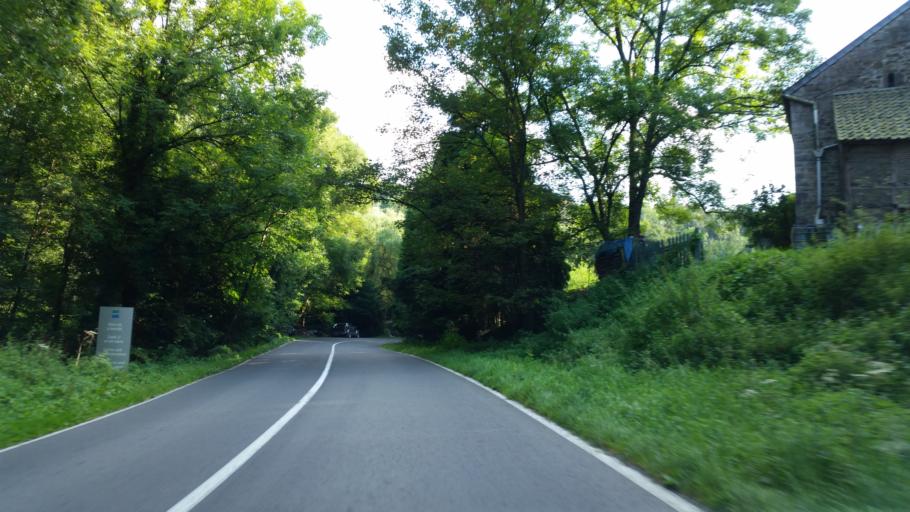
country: BE
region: Wallonia
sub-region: Province de Liege
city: Ouffet
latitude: 50.4100
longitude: 5.4470
